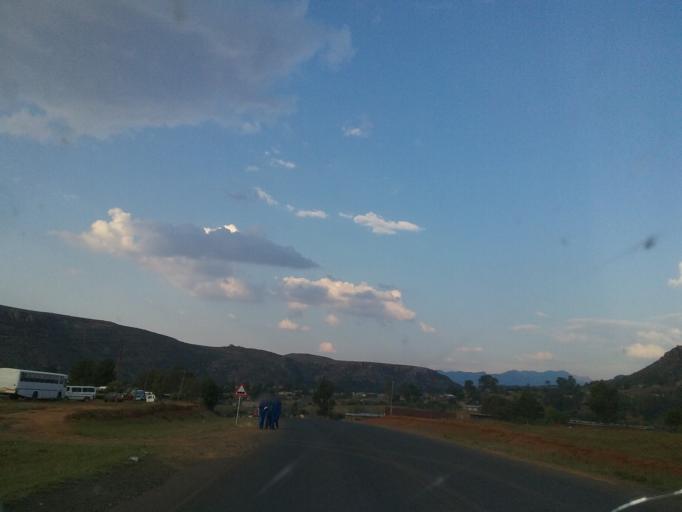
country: LS
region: Quthing
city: Quthing
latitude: -30.3983
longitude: 27.6578
